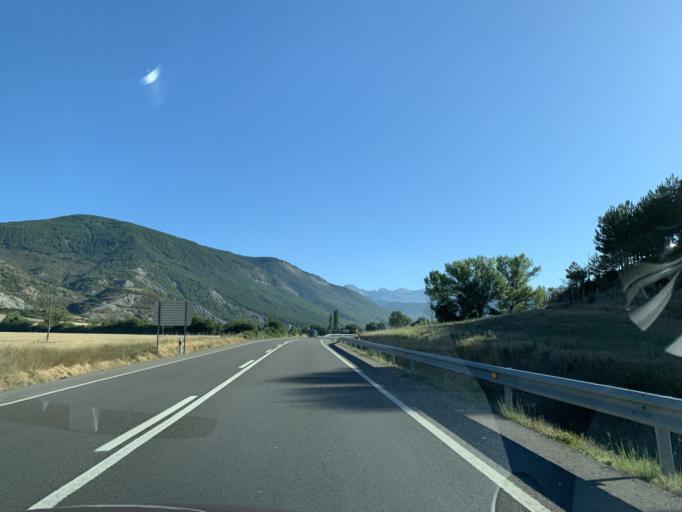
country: ES
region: Aragon
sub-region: Provincia de Huesca
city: Sabinanigo
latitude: 42.5441
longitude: -0.3519
